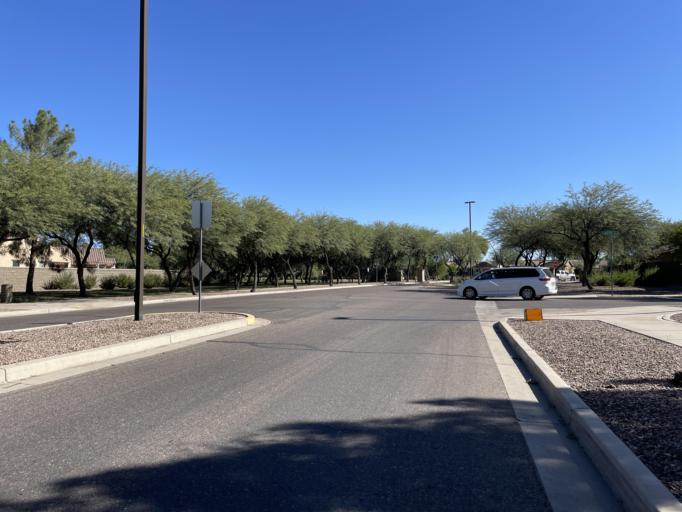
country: US
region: Arizona
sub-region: Maricopa County
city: Queen Creek
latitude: 33.2821
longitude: -111.6922
